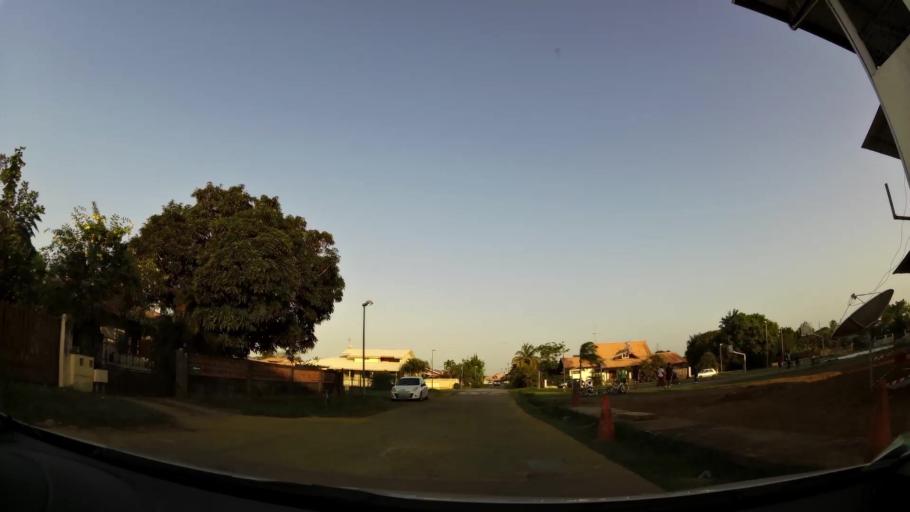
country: GF
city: Macouria
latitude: 5.0094
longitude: -52.4704
